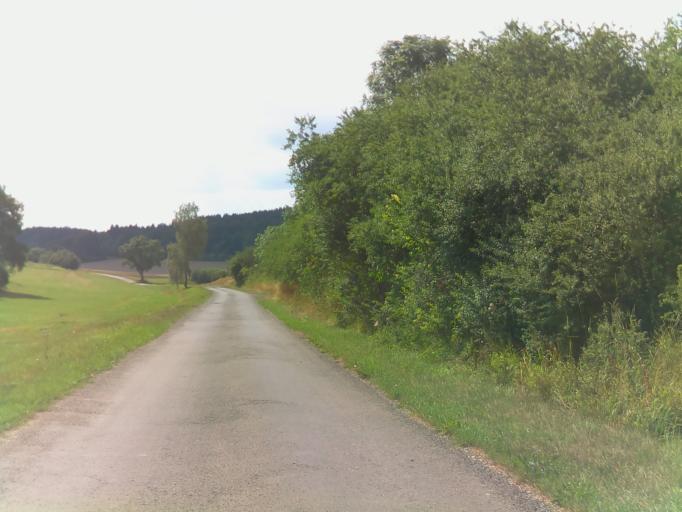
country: DE
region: Thuringia
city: Veilsdorf
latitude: 50.4024
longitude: 10.7973
